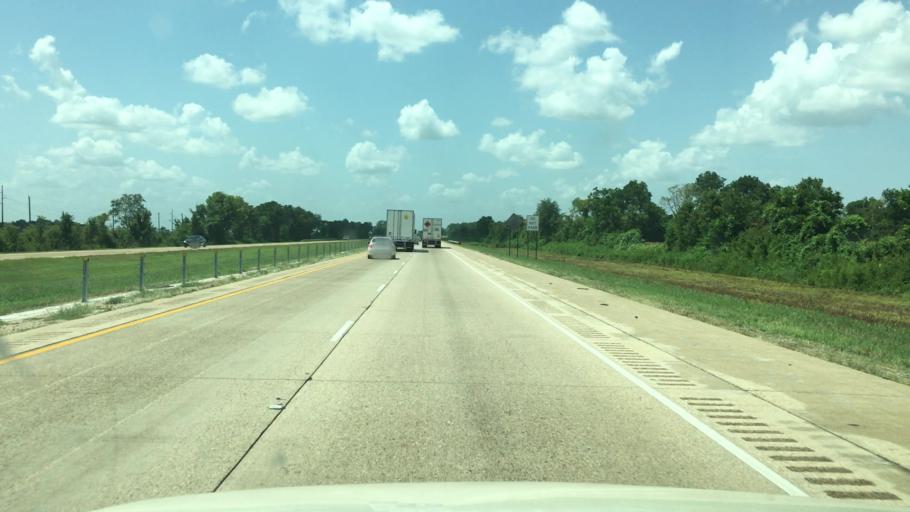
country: US
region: Arkansas
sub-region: Miller County
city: Texarkana
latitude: 33.5627
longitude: -93.8581
